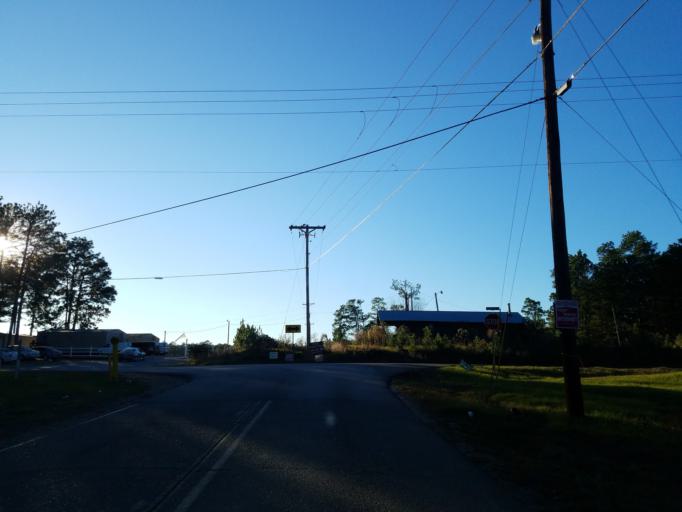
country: US
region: Mississippi
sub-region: Lamar County
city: Arnold Line
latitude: 31.3465
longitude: -89.3986
